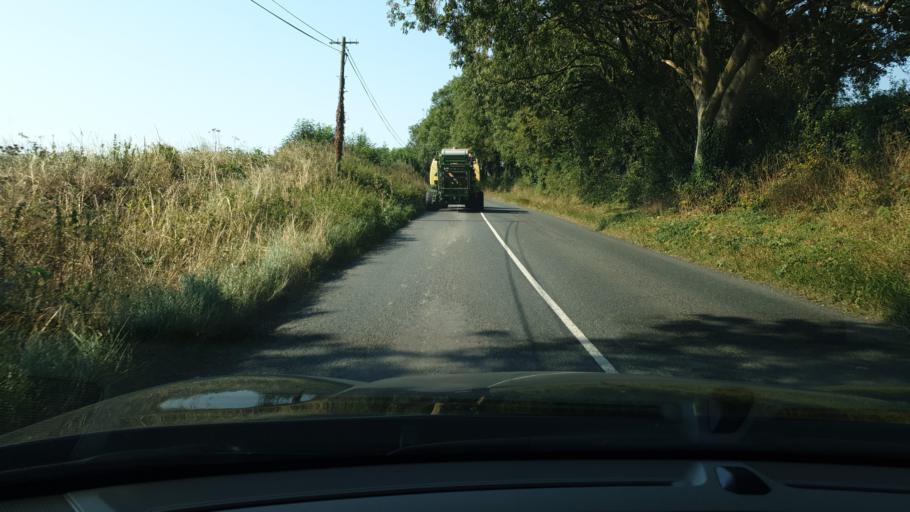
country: IE
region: Leinster
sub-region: An Mhi
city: Athboy
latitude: 53.5942
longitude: -6.8657
